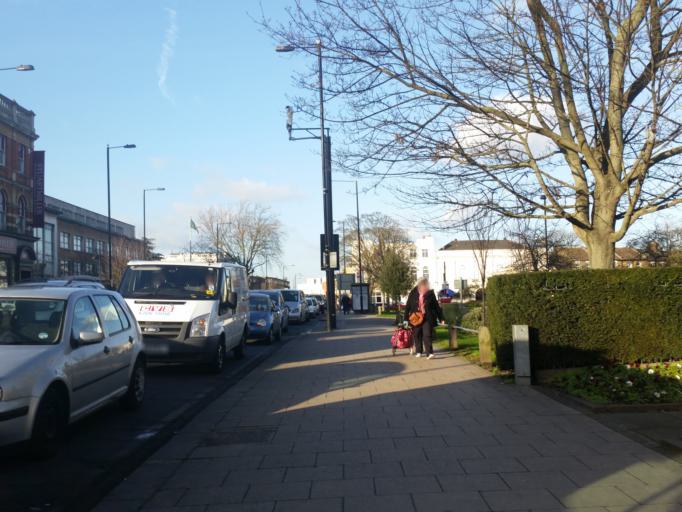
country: GB
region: England
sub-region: Greater London
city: Wood Green
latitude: 51.5994
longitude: -0.1110
